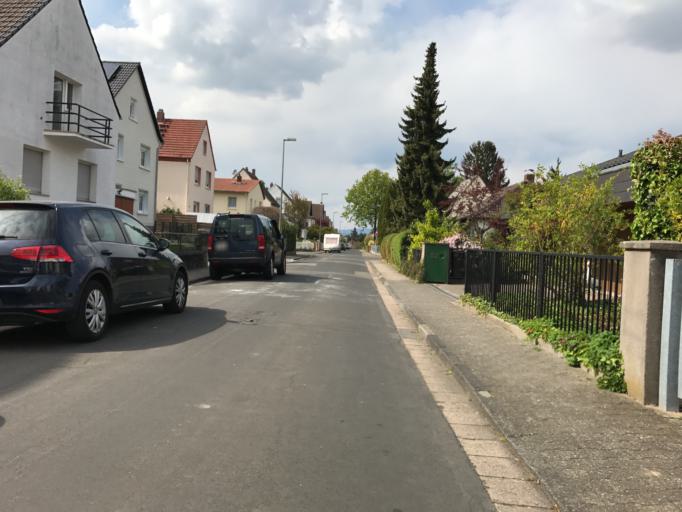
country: DE
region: Rheinland-Pfalz
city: Mainz
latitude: 49.9646
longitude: 8.2749
